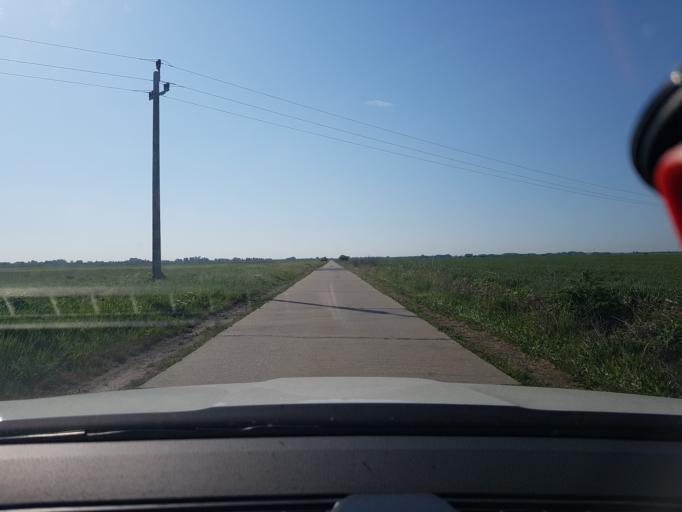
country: HU
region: Tolna
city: Decs
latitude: 46.2827
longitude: 18.6994
